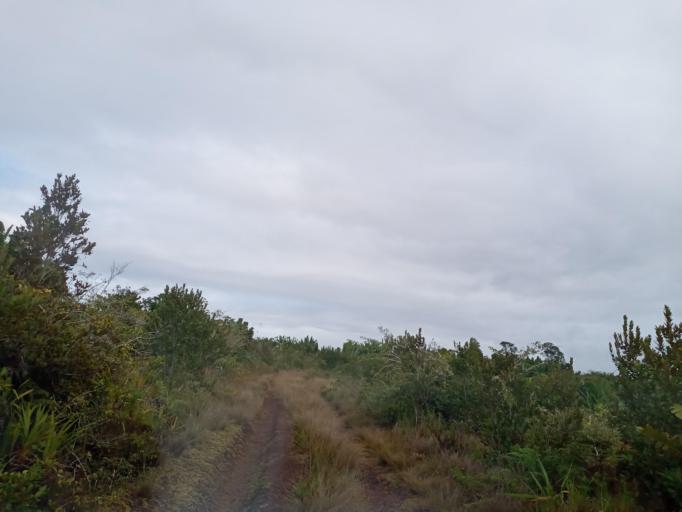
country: MG
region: Atsimo-Atsinanana
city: Vohipaho
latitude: -23.9980
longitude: 47.4041
